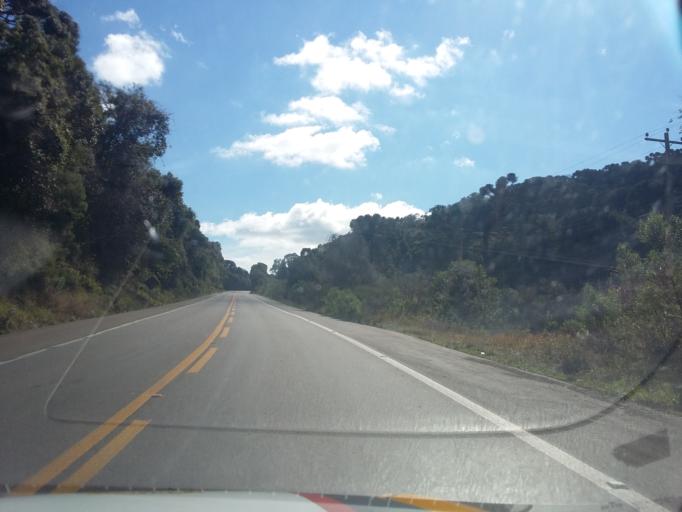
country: BR
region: Rio Grande do Sul
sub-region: Sao Marcos
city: Sao Marcos
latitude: -28.7886
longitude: -51.0951
